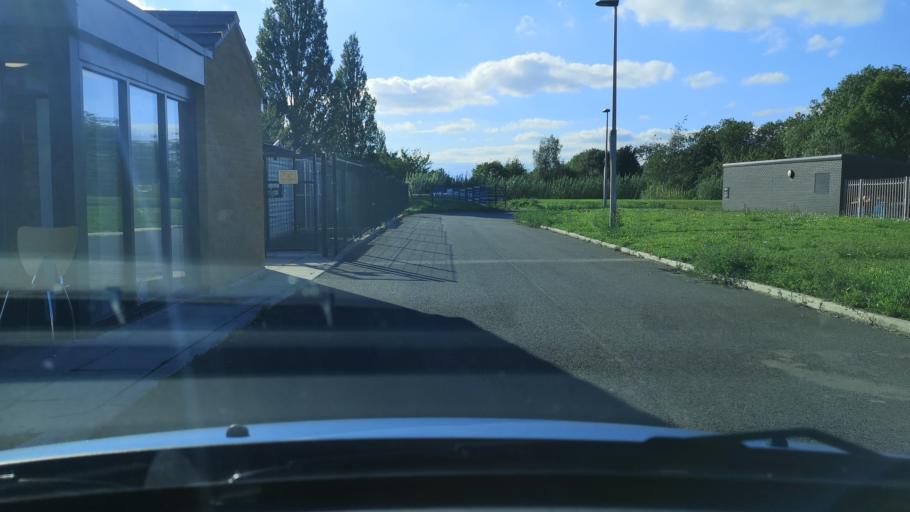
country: GB
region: England
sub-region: North Lincolnshire
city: Scunthorpe
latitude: 53.5769
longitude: -0.6686
